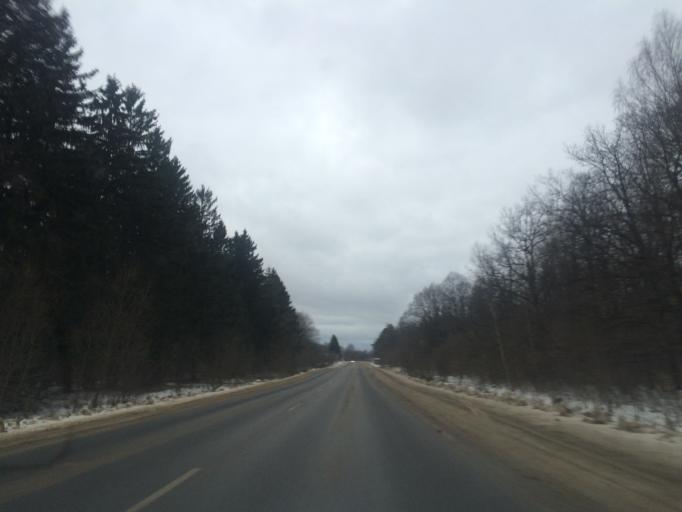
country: RU
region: Tula
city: Odoyev
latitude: 54.0070
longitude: 36.7869
